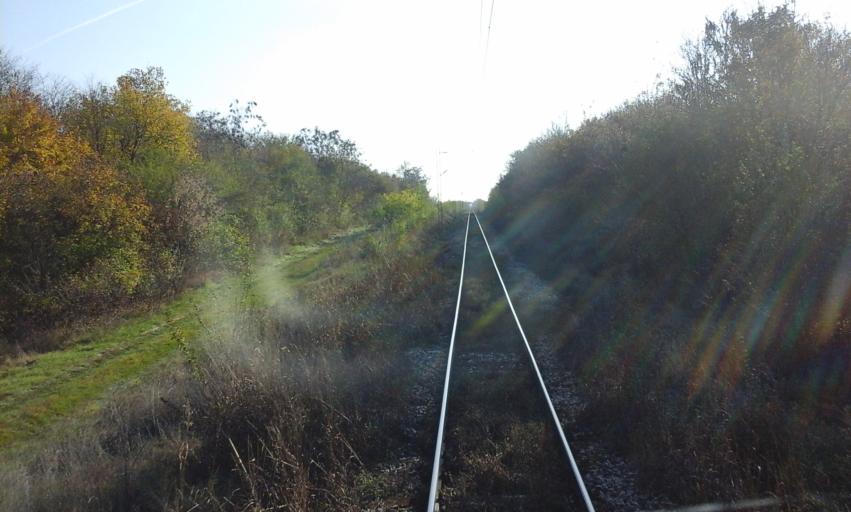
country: RS
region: Autonomna Pokrajina Vojvodina
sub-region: Severnobacki Okrug
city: Mali Igos
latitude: 45.7608
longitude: 19.6484
